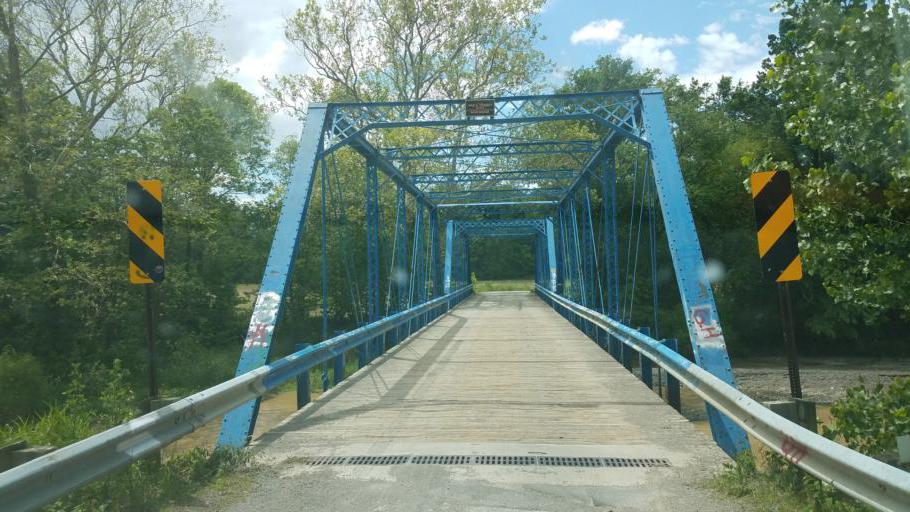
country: US
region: Ohio
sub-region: Huron County
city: Monroeville
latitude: 41.2795
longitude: -82.6750
